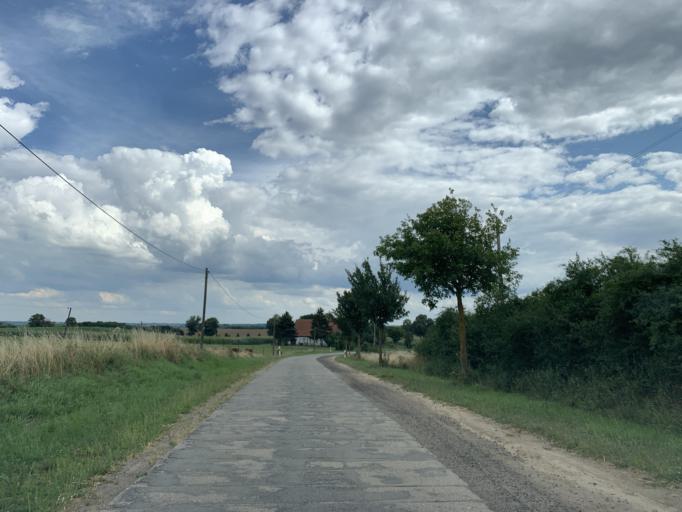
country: DE
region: Mecklenburg-Vorpommern
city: Blankensee
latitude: 53.3741
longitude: 13.2890
